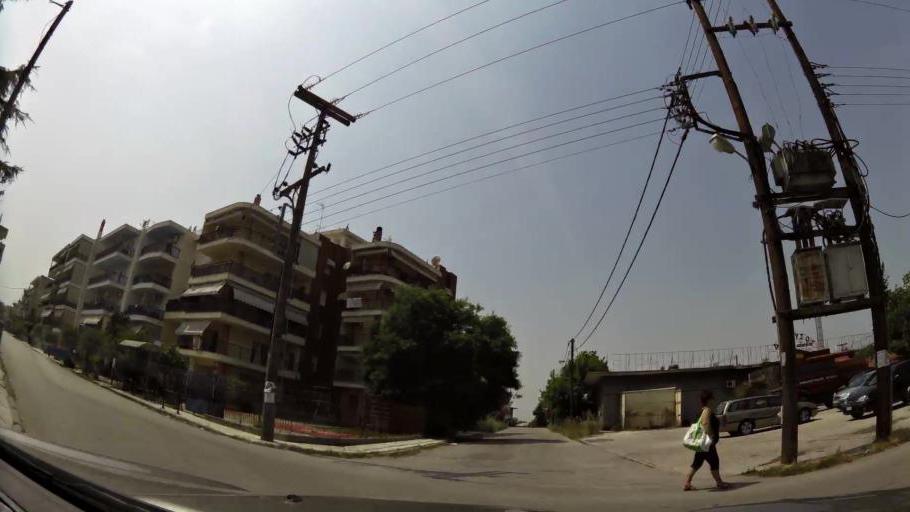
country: GR
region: Central Macedonia
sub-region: Nomos Thessalonikis
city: Diavata
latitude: 40.6911
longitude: 22.8585
